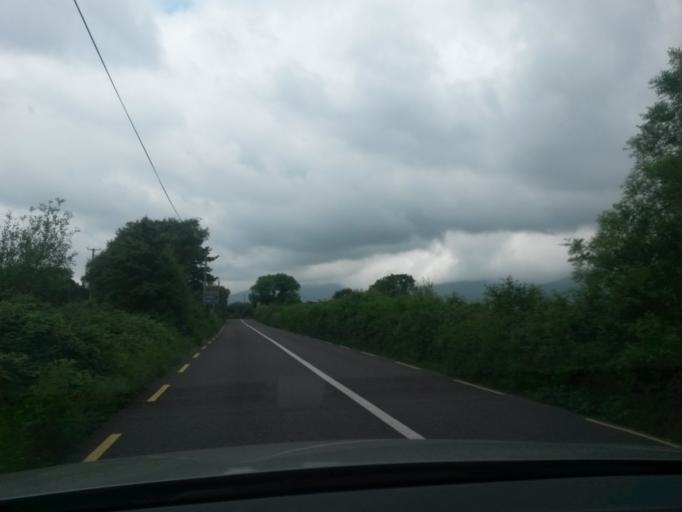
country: IE
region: Munster
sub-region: Ciarrai
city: Tralee
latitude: 52.1635
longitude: -9.6965
